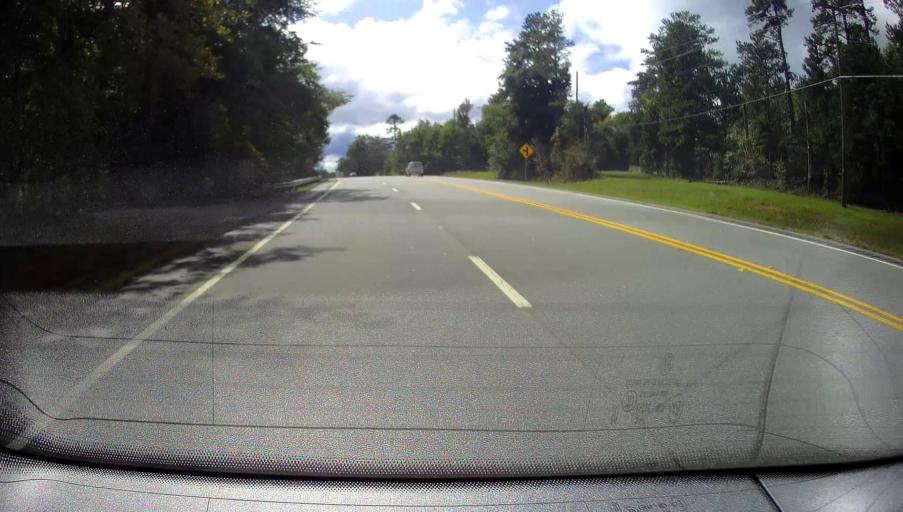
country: US
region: Georgia
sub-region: Baldwin County
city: Milledgeville
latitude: 33.0481
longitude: -83.2926
